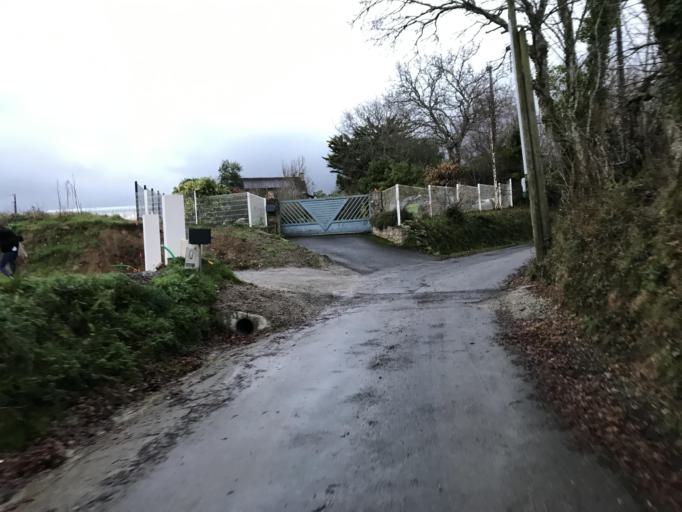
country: FR
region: Brittany
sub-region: Departement du Finistere
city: Plougastel-Daoulas
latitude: 48.3668
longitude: -4.3590
